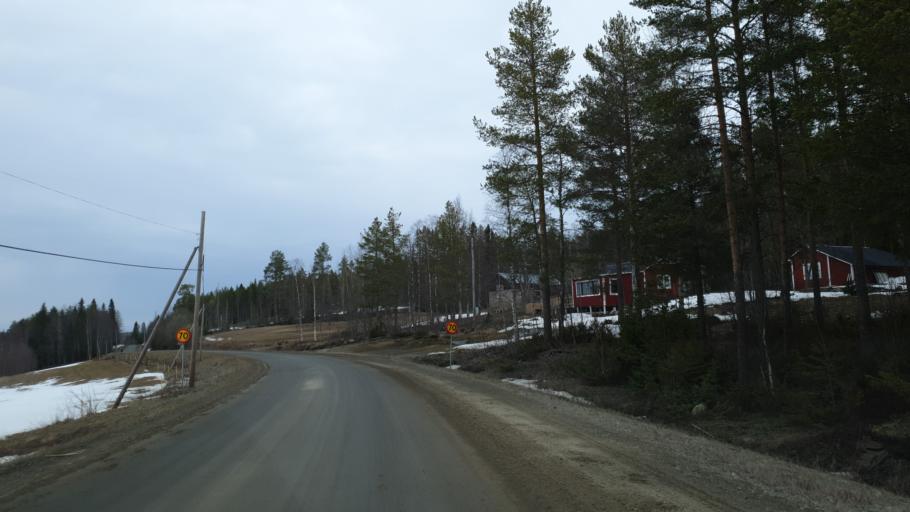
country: SE
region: Vaesterbotten
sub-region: Skelleftea Kommun
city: Burea
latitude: 64.3180
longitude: 21.1391
